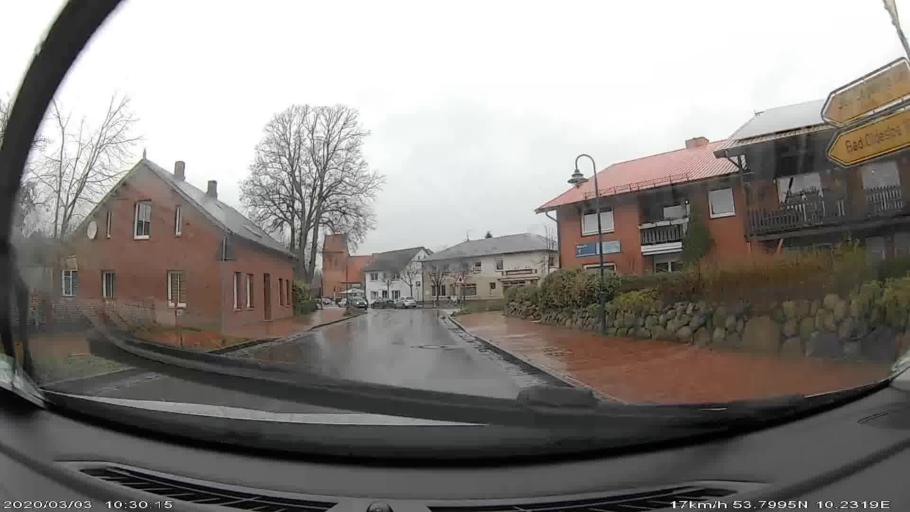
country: DE
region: Schleswig-Holstein
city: Sulfeld
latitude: 53.8009
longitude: 10.2305
